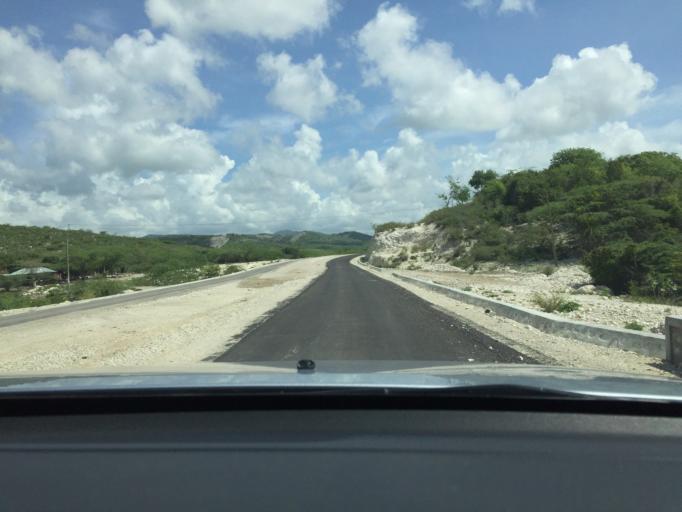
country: HT
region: Sud
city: Aquin
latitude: 18.2359
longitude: -73.2845
